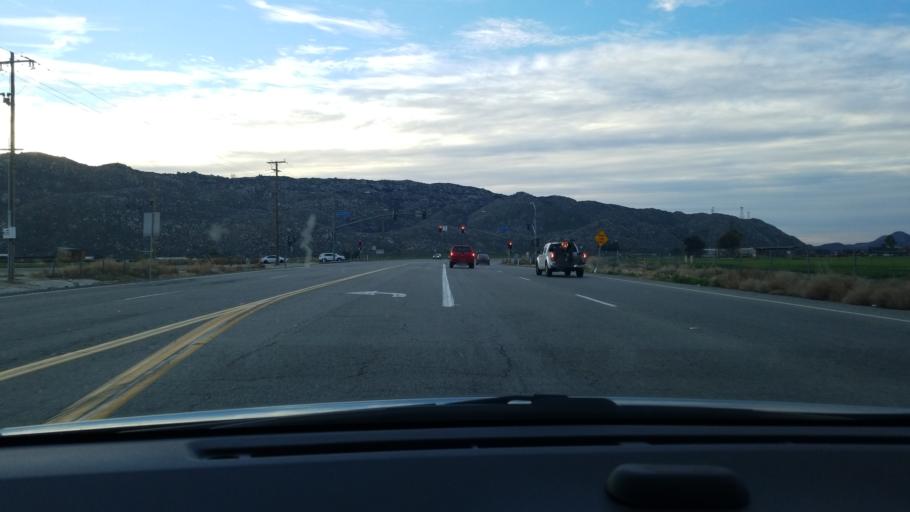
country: US
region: California
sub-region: Riverside County
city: San Jacinto
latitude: 33.8235
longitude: -117.0324
